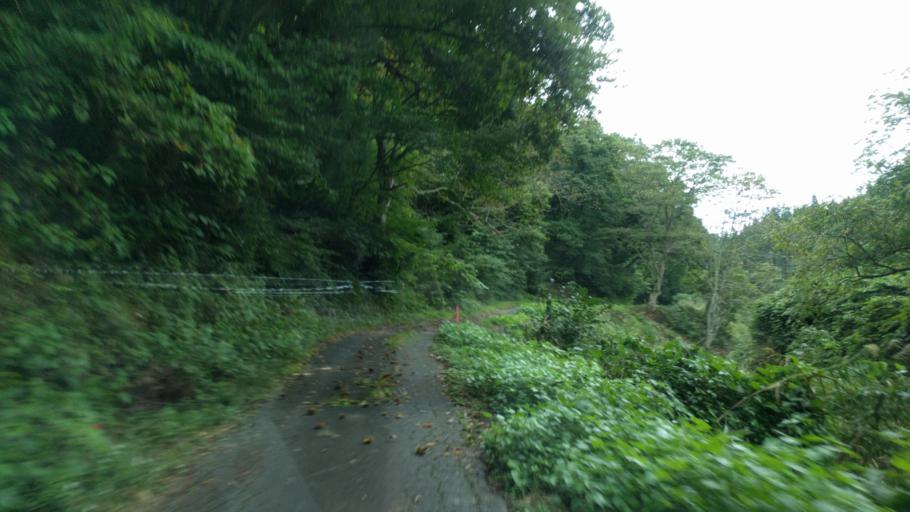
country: JP
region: Fukushima
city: Kitakata
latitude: 37.5247
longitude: 139.7588
